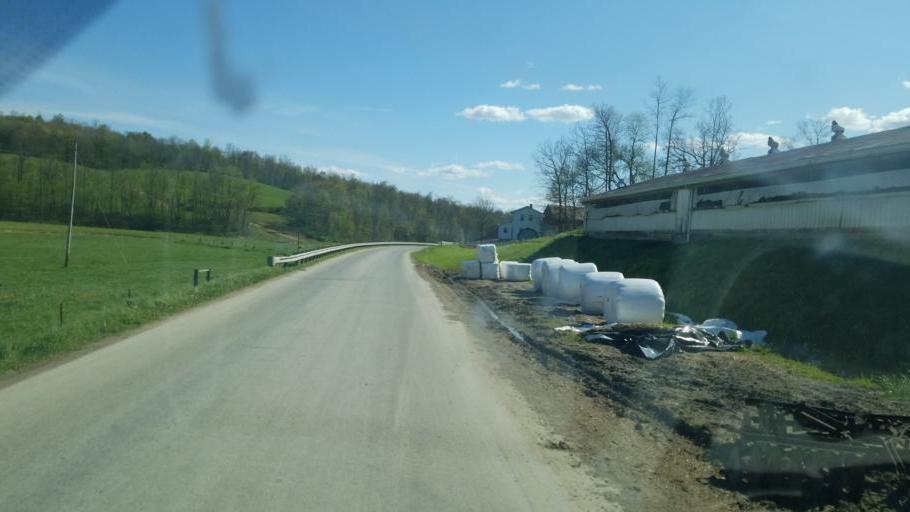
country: US
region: Ohio
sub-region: Coshocton County
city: Coshocton
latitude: 40.4227
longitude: -81.8274
